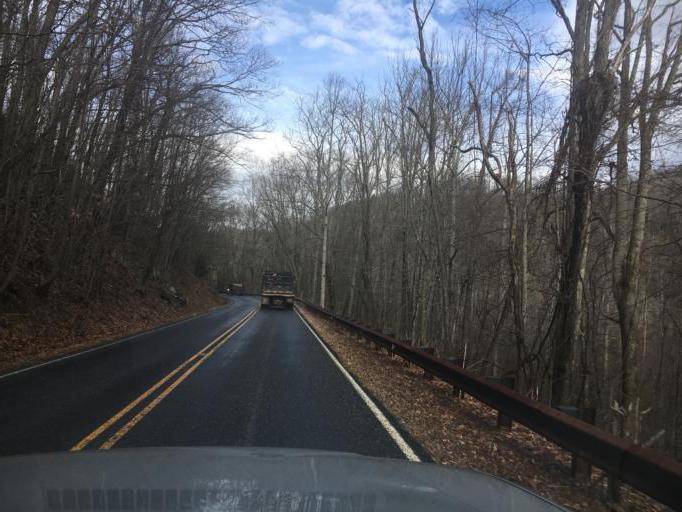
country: US
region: North Carolina
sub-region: Haywood County
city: Canton
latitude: 35.3781
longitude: -82.8092
